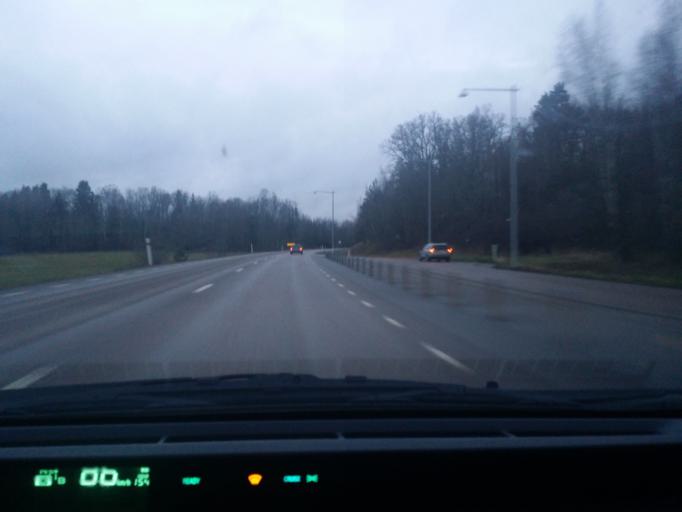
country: SE
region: Soedermanland
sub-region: Eskilstuna Kommun
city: Kvicksund
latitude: 59.4726
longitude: 16.3074
